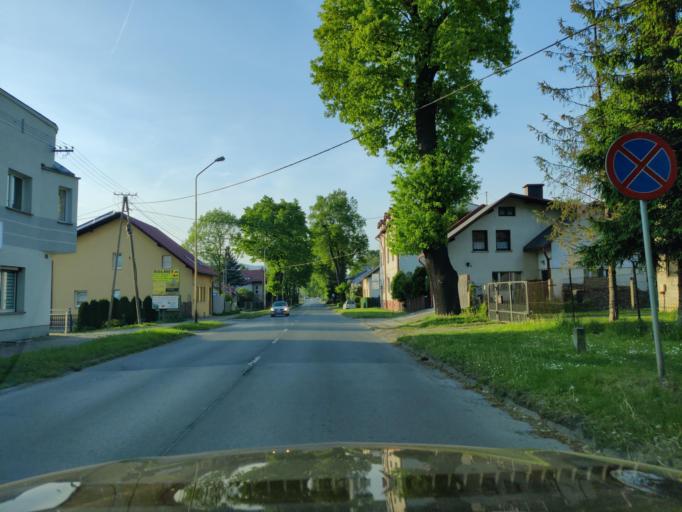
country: PL
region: Silesian Voivodeship
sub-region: Powiat zywiecki
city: Zywiec
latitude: 49.6964
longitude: 19.2024
